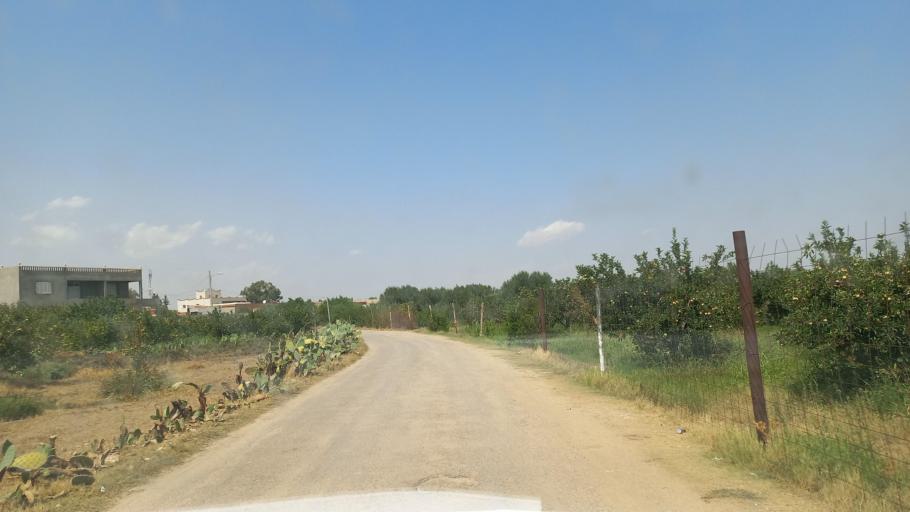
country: TN
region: Al Qasrayn
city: Kasserine
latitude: 35.2477
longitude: 9.0281
